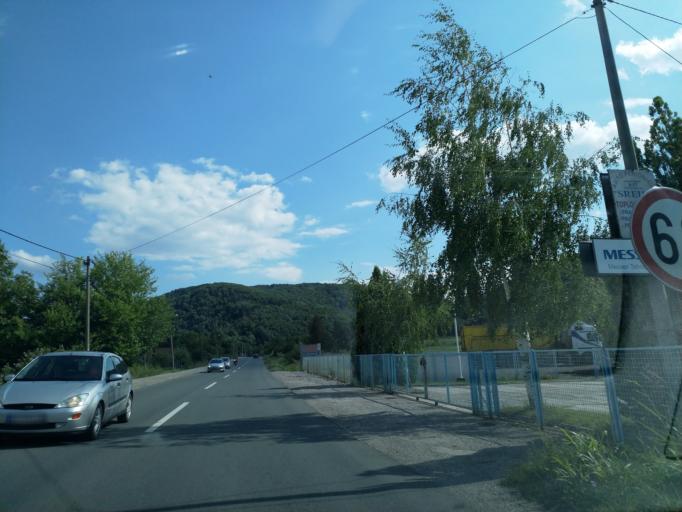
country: RS
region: Central Serbia
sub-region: Rasinski Okrug
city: Trstenik
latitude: 43.6235
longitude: 20.9760
